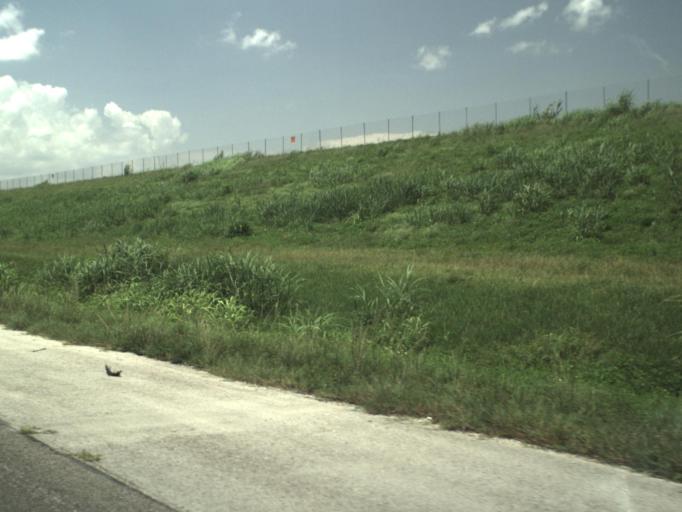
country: US
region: Florida
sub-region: Palm Beach County
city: South Bay
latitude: 26.6842
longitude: -80.7547
